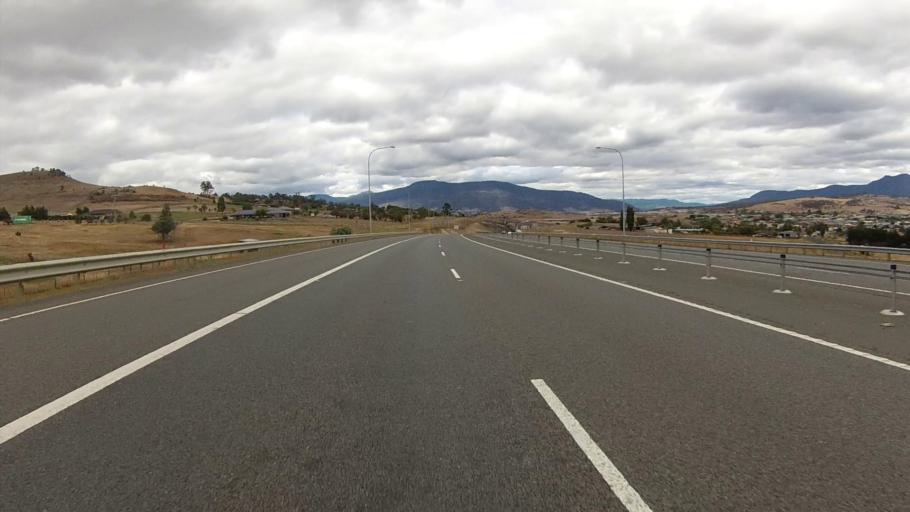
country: AU
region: Tasmania
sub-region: Brighton
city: Bridgewater
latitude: -42.6998
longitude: 147.2753
